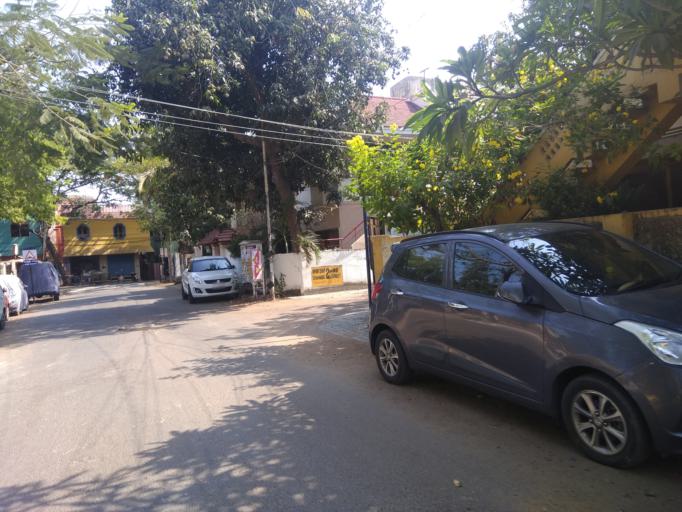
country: IN
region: Tamil Nadu
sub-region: Kancheepuram
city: Perungudi
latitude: 12.9861
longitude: 80.2298
